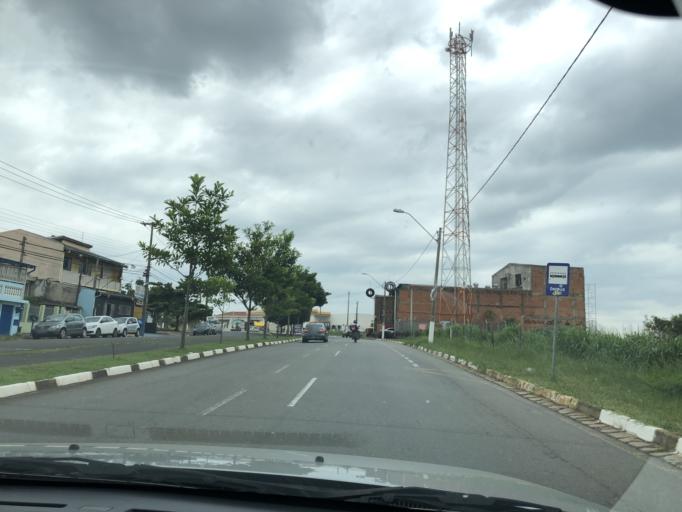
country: BR
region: Sao Paulo
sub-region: Paulinia
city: Paulinia
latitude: -22.7498
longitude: -47.1696
